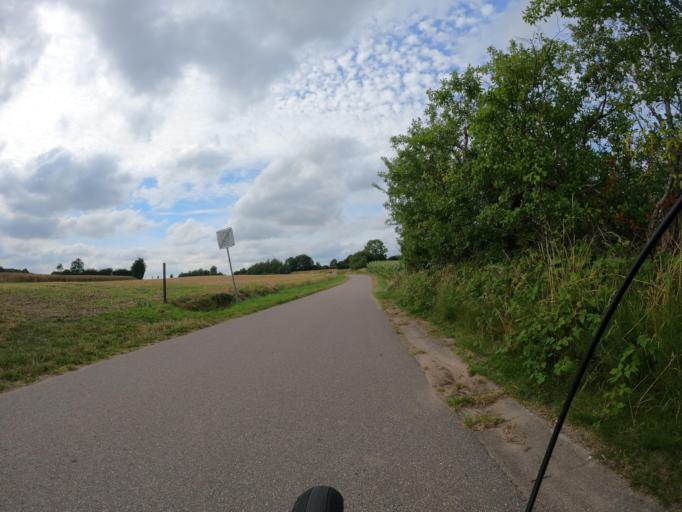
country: DE
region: Schleswig-Holstein
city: Niesgrau
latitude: 54.7442
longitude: 9.7980
